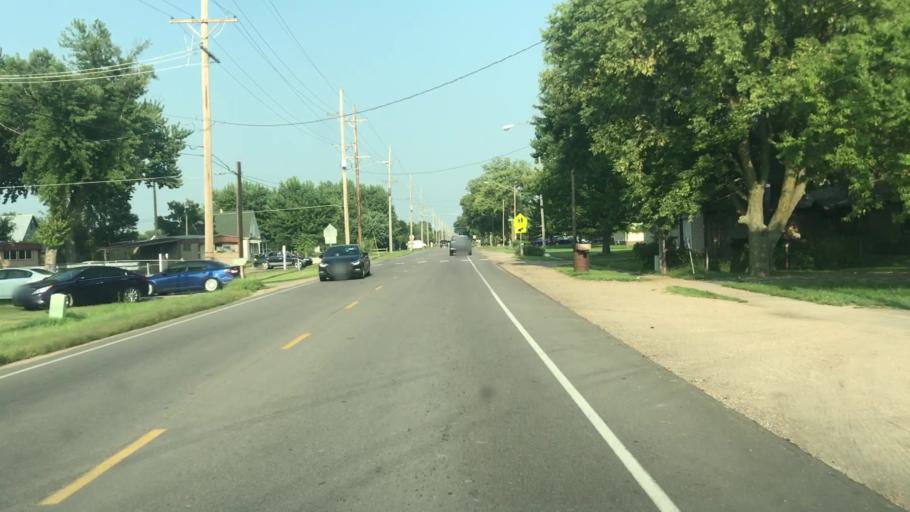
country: US
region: Nebraska
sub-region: Hall County
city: Grand Island
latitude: 40.9457
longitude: -98.3460
